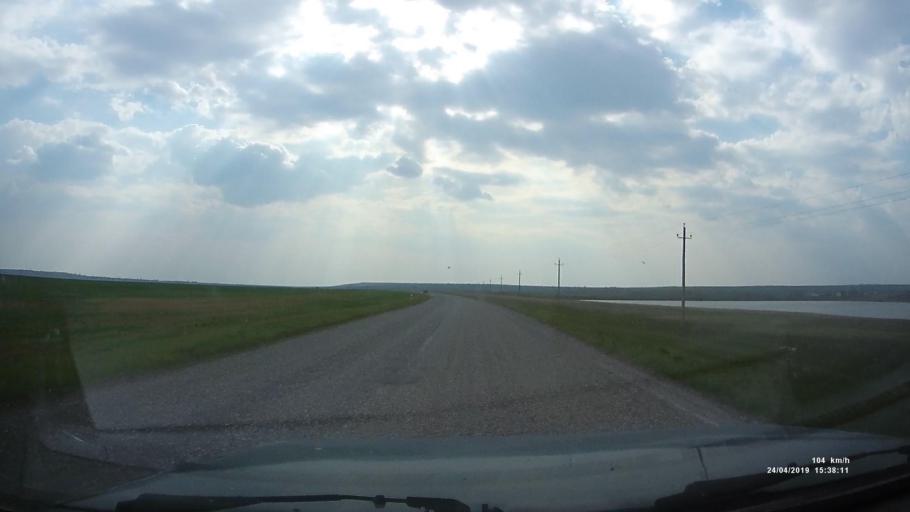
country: RU
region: Kalmykiya
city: Yashalta
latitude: 46.5995
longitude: 42.8328
